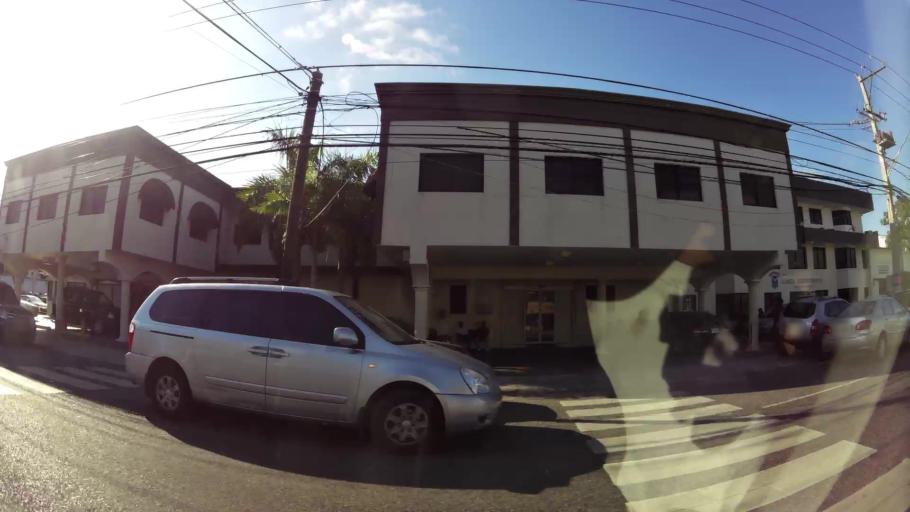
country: DO
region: Nacional
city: Bella Vista
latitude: 18.4480
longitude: -69.9320
